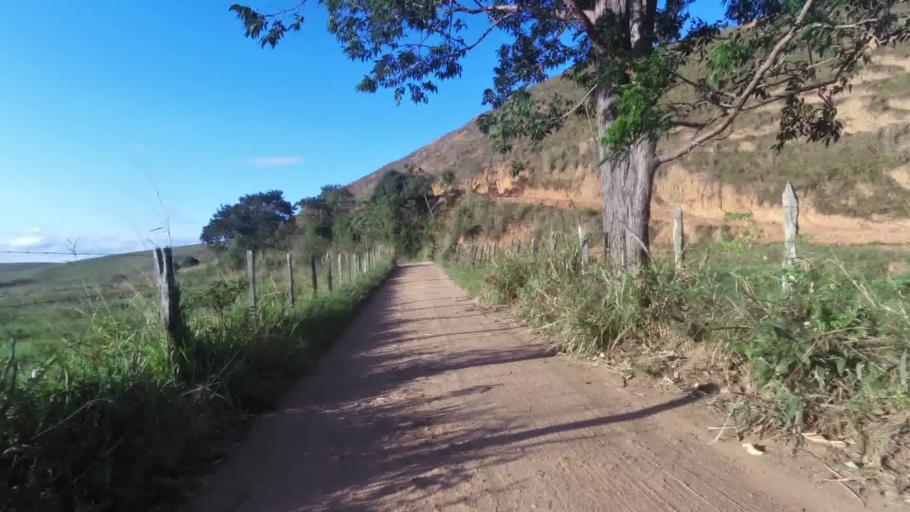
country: BR
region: Espirito Santo
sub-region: Marataizes
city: Marataizes
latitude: -21.1405
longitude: -41.0185
